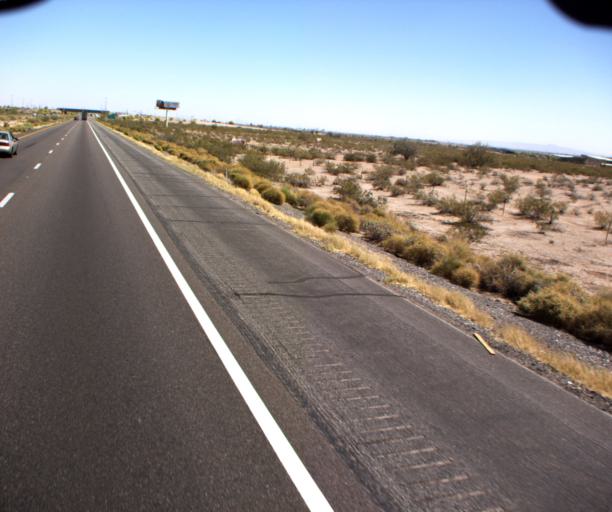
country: US
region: Arizona
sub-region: Maricopa County
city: Buckeye
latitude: 33.4575
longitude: -112.5163
